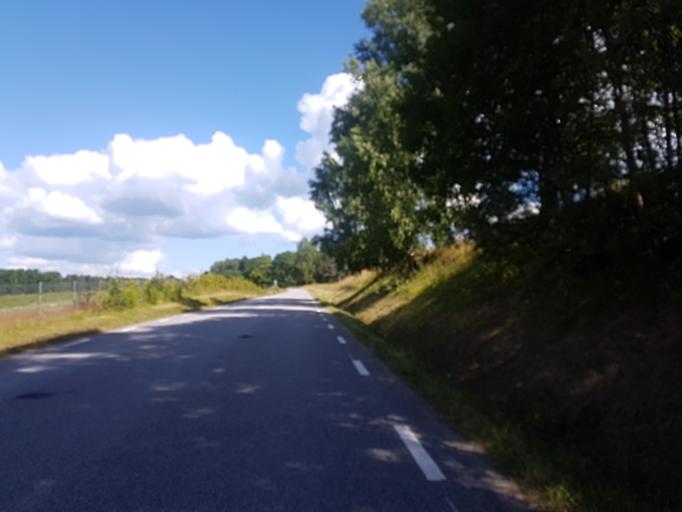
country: SE
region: Soedermanland
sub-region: Gnesta Kommun
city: Gnesta
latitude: 59.0468
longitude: 17.3383
